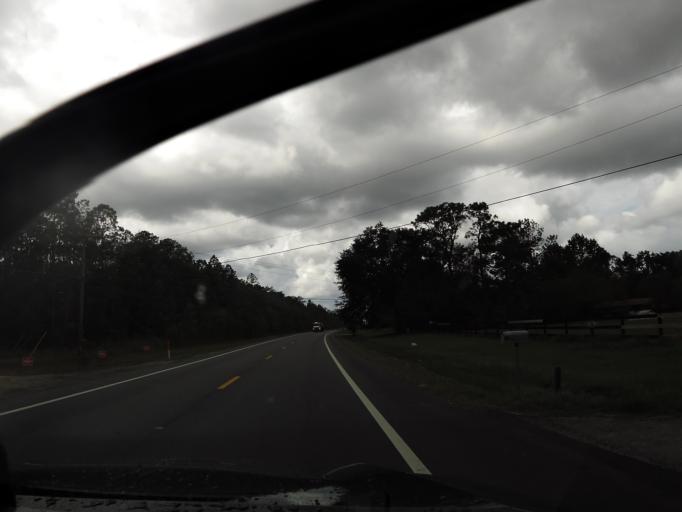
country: US
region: Florida
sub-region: Clay County
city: Asbury Lake
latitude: 30.0339
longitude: -81.8248
